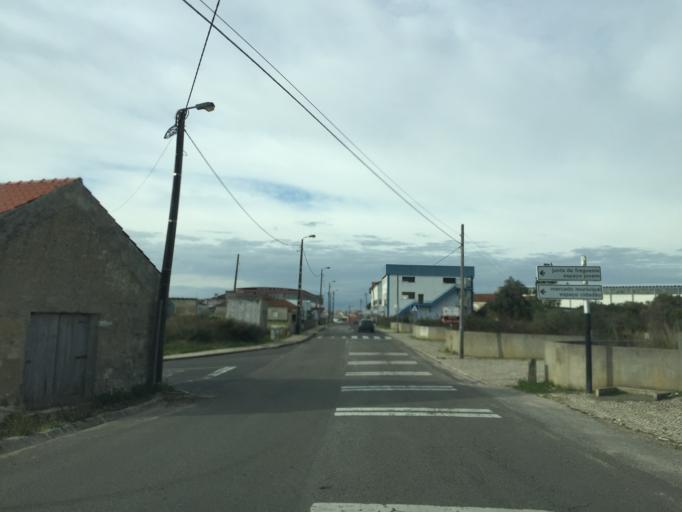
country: PT
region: Lisbon
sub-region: Sintra
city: Pero Pinheiro
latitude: 38.8603
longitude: -9.3214
